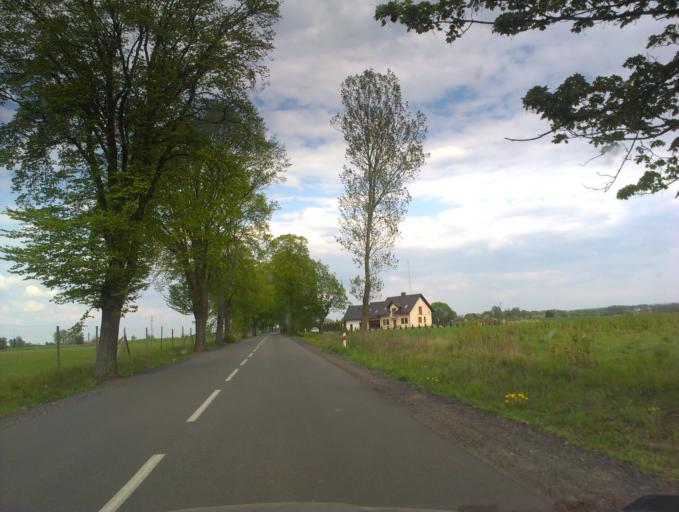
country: PL
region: Pomeranian Voivodeship
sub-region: Powiat czluchowski
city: Czarne
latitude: 53.6847
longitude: 16.9605
